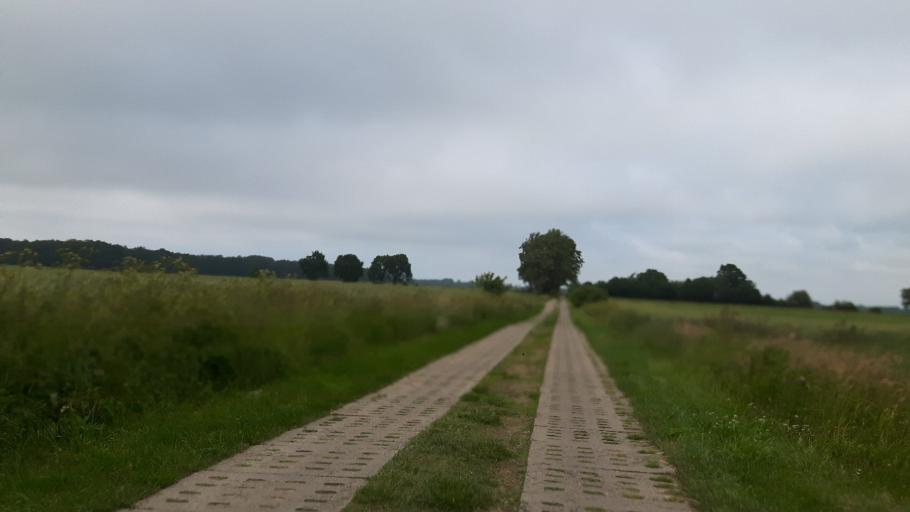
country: PL
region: West Pomeranian Voivodeship
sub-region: Powiat koszalinski
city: Sianow
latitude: 54.3052
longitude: 16.2849
